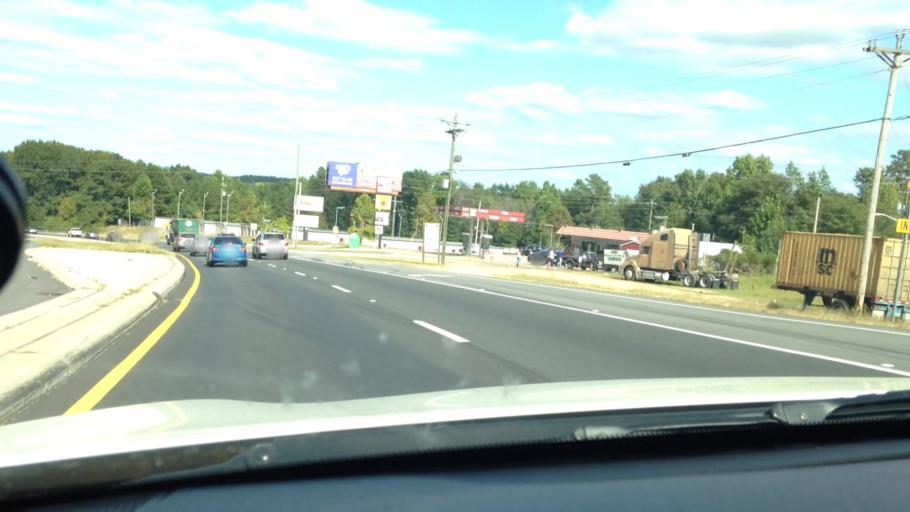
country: US
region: Georgia
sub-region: Richmond County
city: Hephzibah
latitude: 33.4104
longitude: -82.0900
